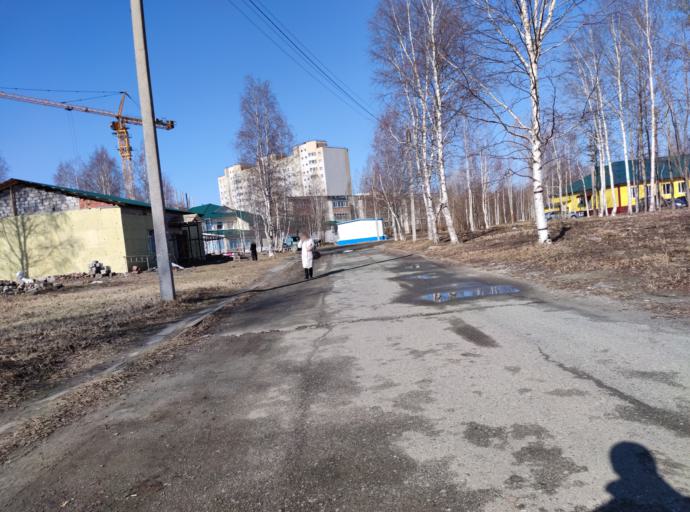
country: RU
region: Khanty-Mansiyskiy Avtonomnyy Okrug
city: Langepas
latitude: 61.2514
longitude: 75.1693
